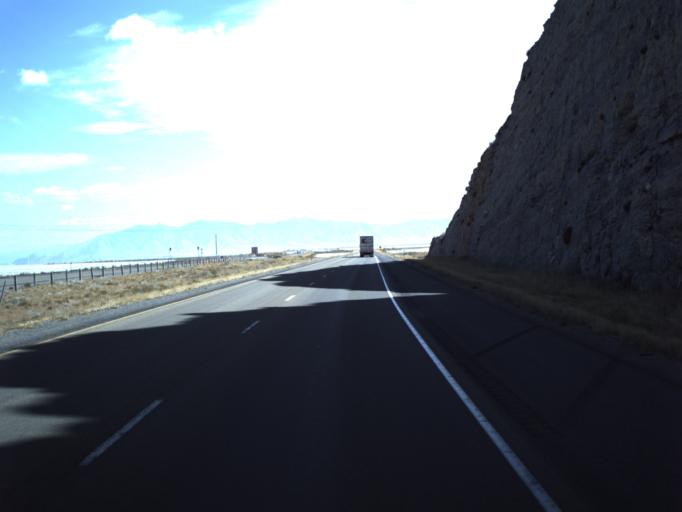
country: US
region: Utah
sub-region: Tooele County
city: Grantsville
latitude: 40.7438
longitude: -112.6347
